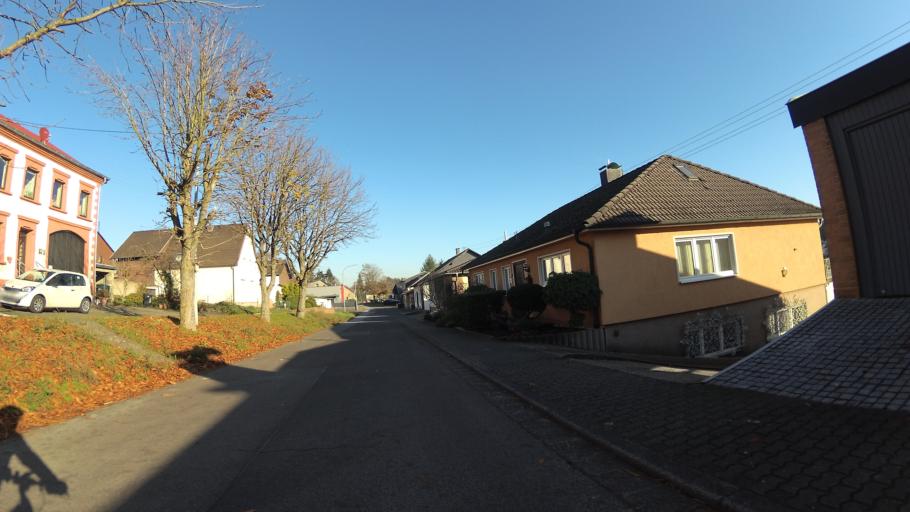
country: DE
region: Saarland
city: Bous
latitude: 49.2959
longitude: 6.8003
